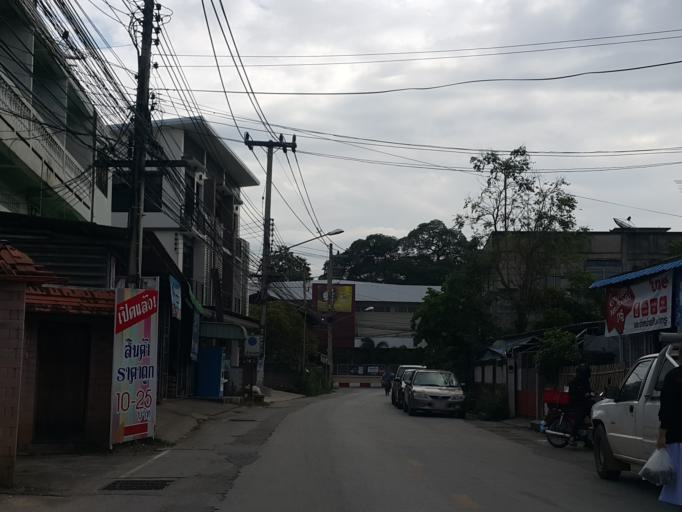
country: TH
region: Lampang
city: Lampang
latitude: 18.2946
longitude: 99.5012
